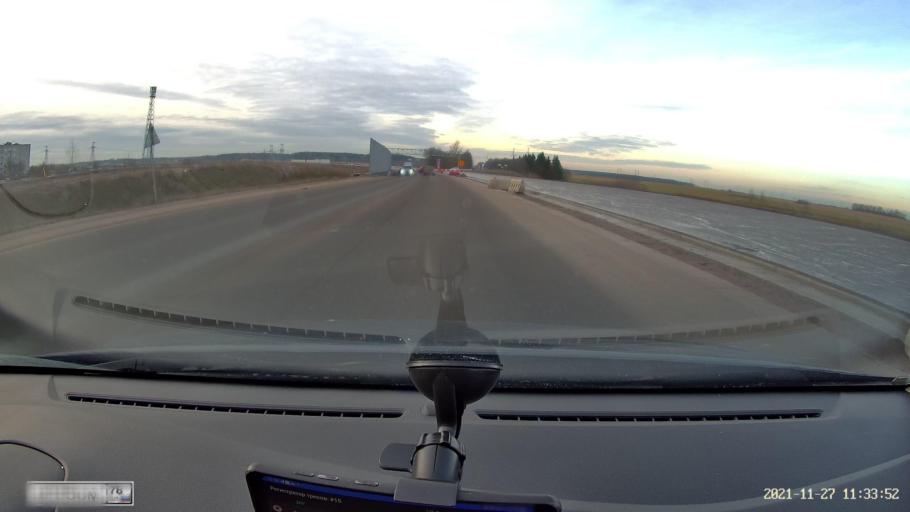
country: RU
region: Leningrad
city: Russko-Vysotskoye
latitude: 59.7086
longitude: 30.0102
